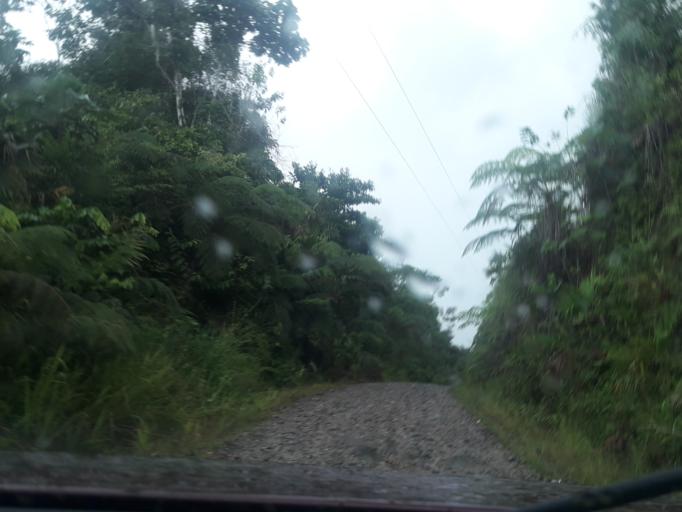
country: EC
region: Napo
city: Tena
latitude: -1.0998
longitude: -77.6894
